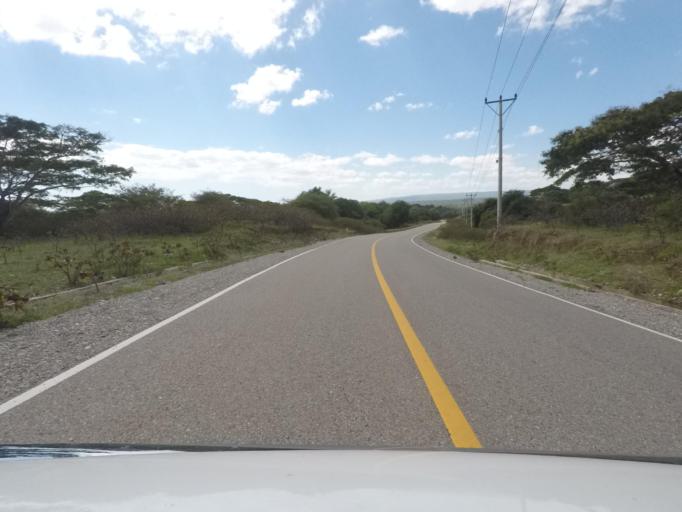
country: TL
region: Lautem
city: Lospalos
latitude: -8.4039
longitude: 126.8205
